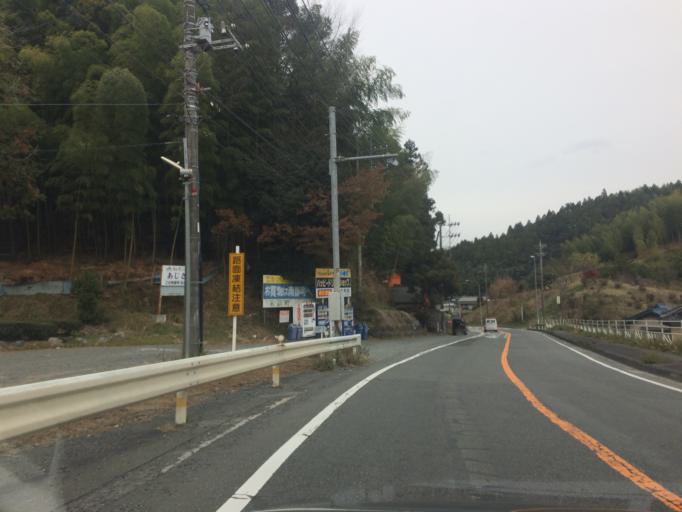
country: JP
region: Shizuoka
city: Fujinomiya
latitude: 35.2756
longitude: 138.4503
